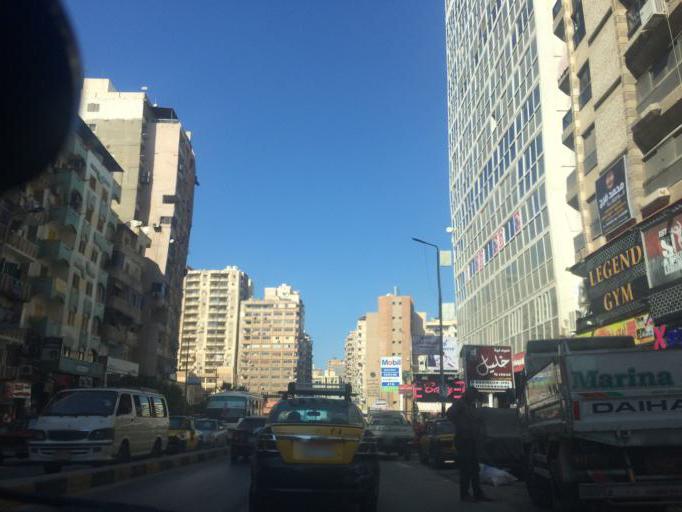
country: EG
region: Alexandria
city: Alexandria
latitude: 31.2645
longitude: 29.9966
